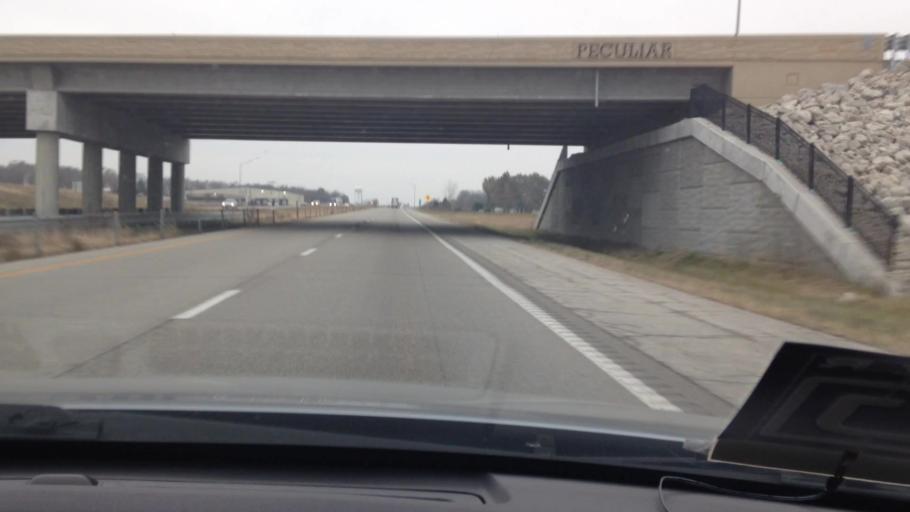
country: US
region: Missouri
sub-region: Cass County
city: Peculiar
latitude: 38.7393
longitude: -94.4701
